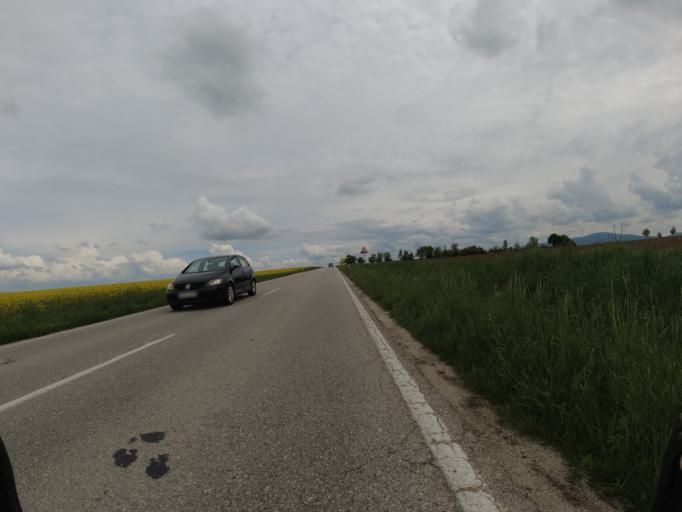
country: SK
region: Nitriansky
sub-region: Okres Nitra
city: Nitra
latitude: 48.5288
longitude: 18.0879
